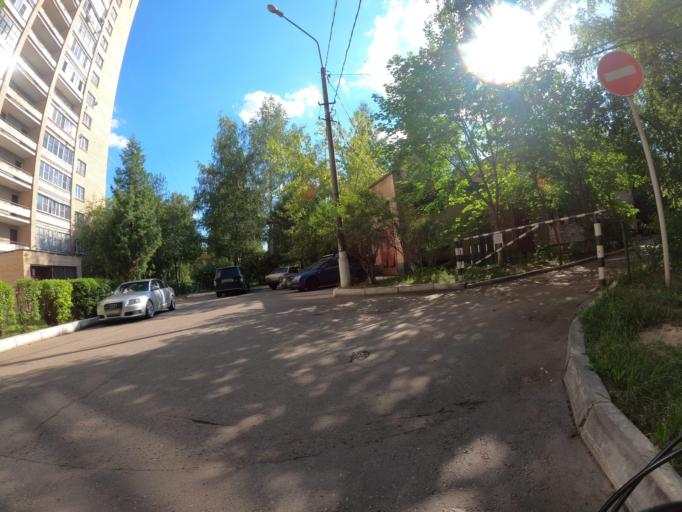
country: RU
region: Moskovskaya
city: Stupino
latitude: 54.8870
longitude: 38.0580
